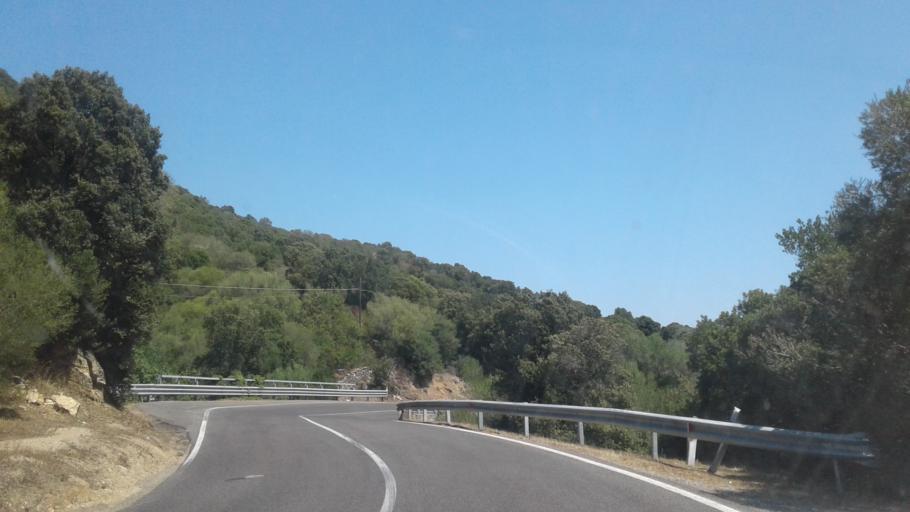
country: IT
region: Sardinia
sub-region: Provincia di Olbia-Tempio
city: Telti
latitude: 40.9057
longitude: 9.3951
